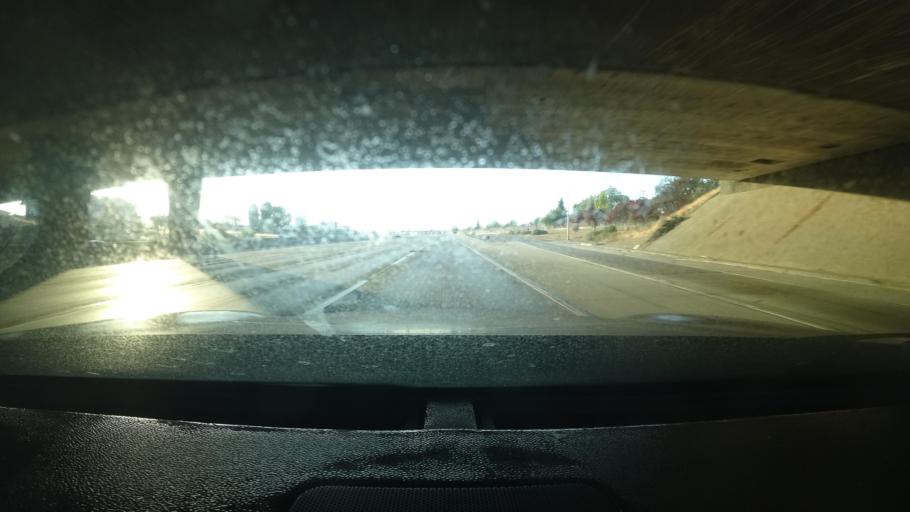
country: US
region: California
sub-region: Santa Clara County
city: San Jose
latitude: 37.3498
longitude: -121.8613
